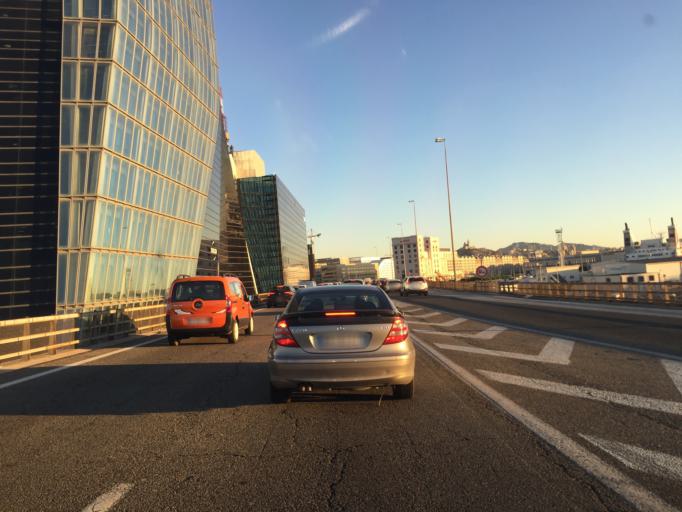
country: FR
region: Provence-Alpes-Cote d'Azur
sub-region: Departement des Bouches-du-Rhone
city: Marseille 03
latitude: 43.3157
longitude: 5.3650
